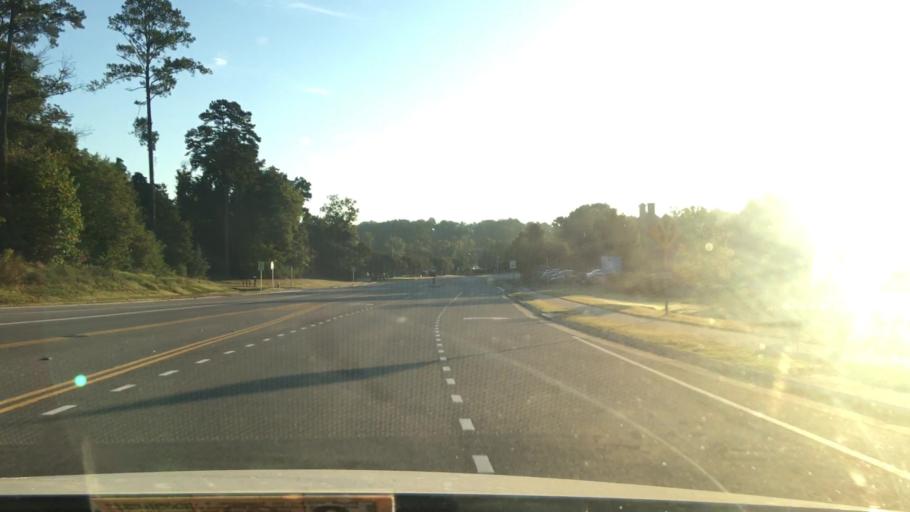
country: US
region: Virginia
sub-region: Henrico County
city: Tuckahoe
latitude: 37.5671
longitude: -77.5404
